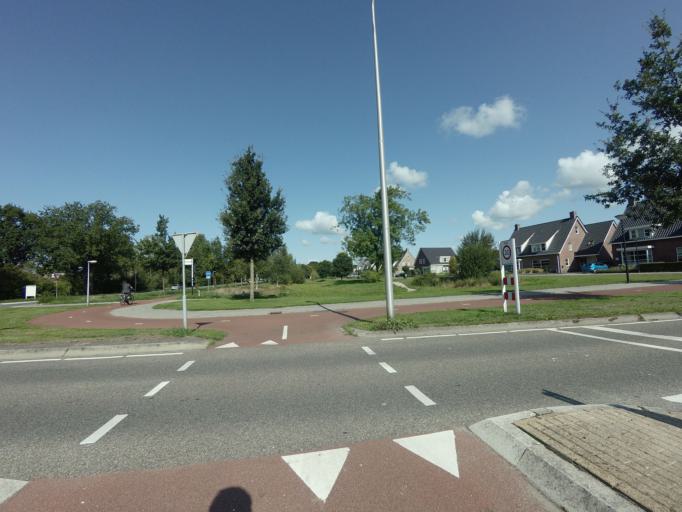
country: NL
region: Overijssel
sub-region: Gemeente Dalfsen
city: Dalfsen
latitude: 52.5132
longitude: 6.2621
